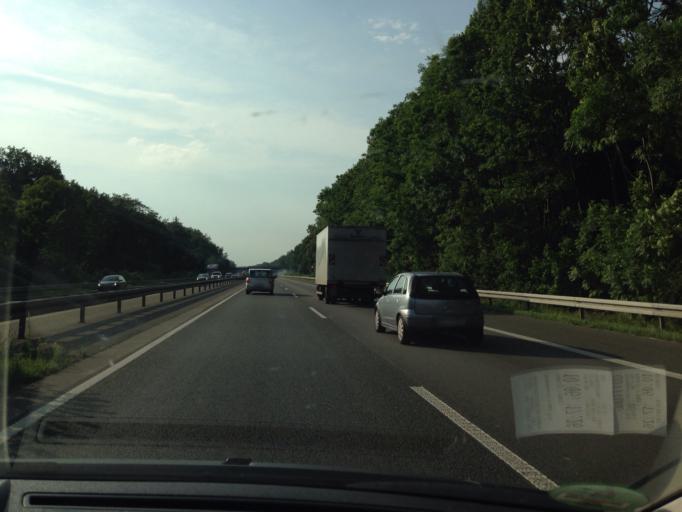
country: DE
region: North Rhine-Westphalia
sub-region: Regierungsbezirk Munster
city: Ascheberg
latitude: 51.8185
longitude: 7.6142
